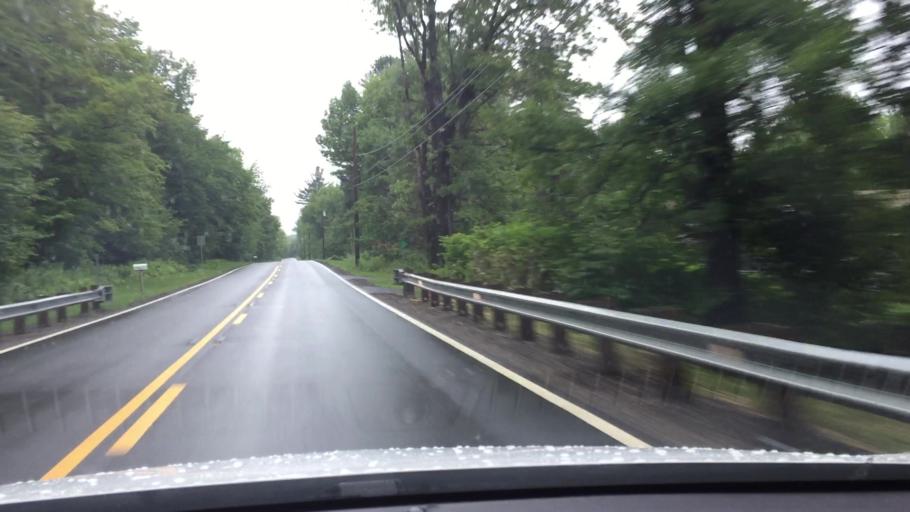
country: US
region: Massachusetts
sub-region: Berkshire County
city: Becket
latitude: 42.3504
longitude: -73.1253
